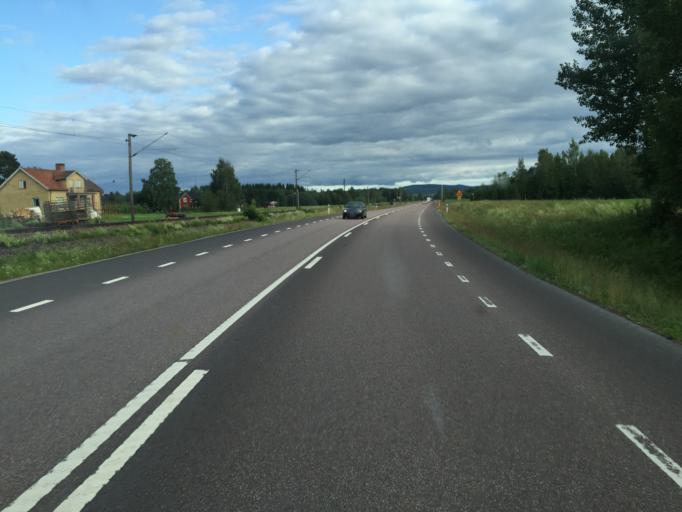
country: SE
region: Dalarna
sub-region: Gagnefs Kommun
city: Djuras
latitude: 60.5772
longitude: 15.1220
